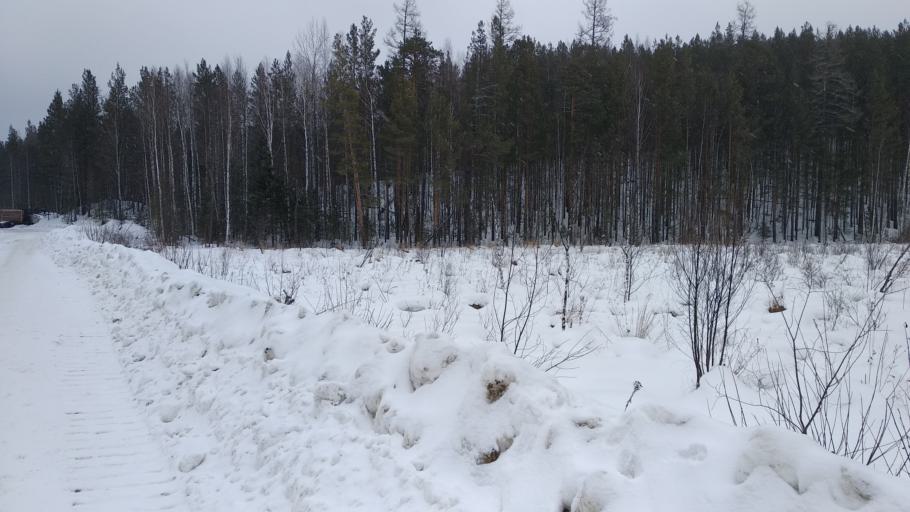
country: RU
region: Sverdlovsk
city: Karpinsk
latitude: 59.6982
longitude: 59.6063
